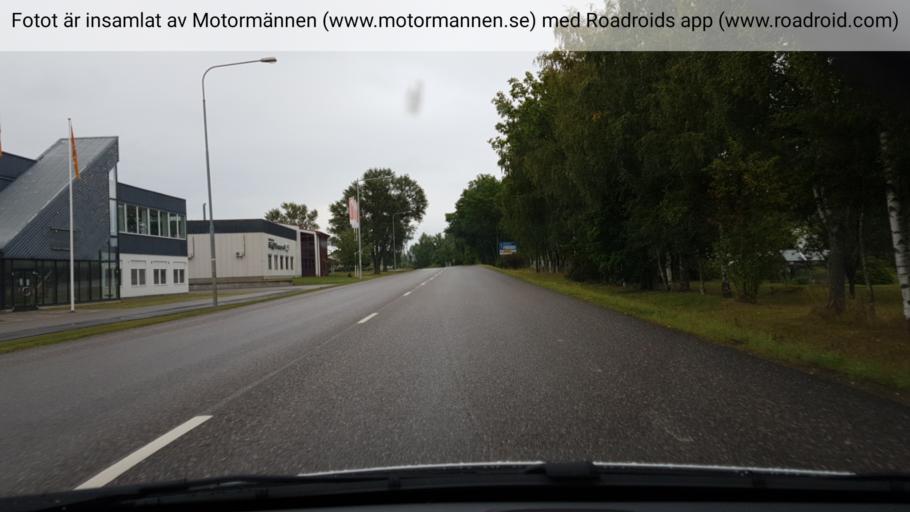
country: SE
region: Vaestra Goetaland
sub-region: Tibro Kommun
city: Tibro
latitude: 58.4235
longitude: 14.1366
